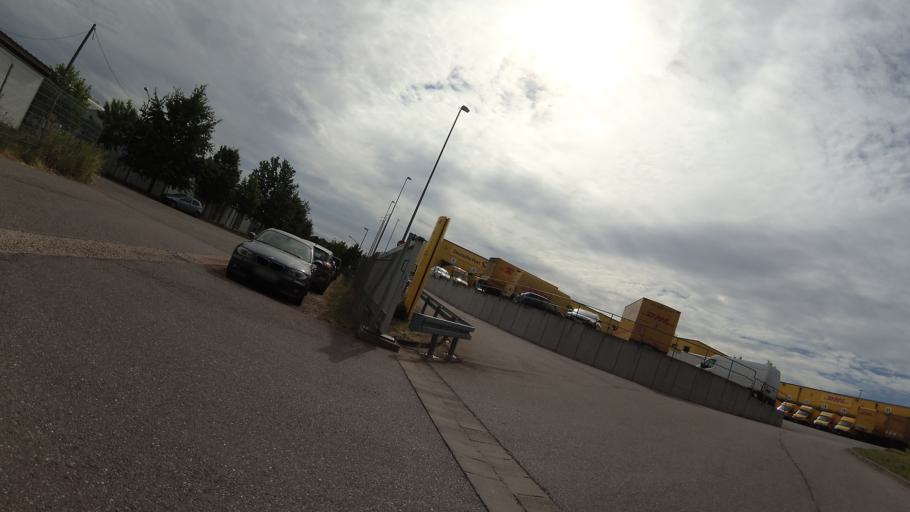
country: DE
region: Saarland
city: Schwalbach
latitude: 49.3243
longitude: 6.8106
